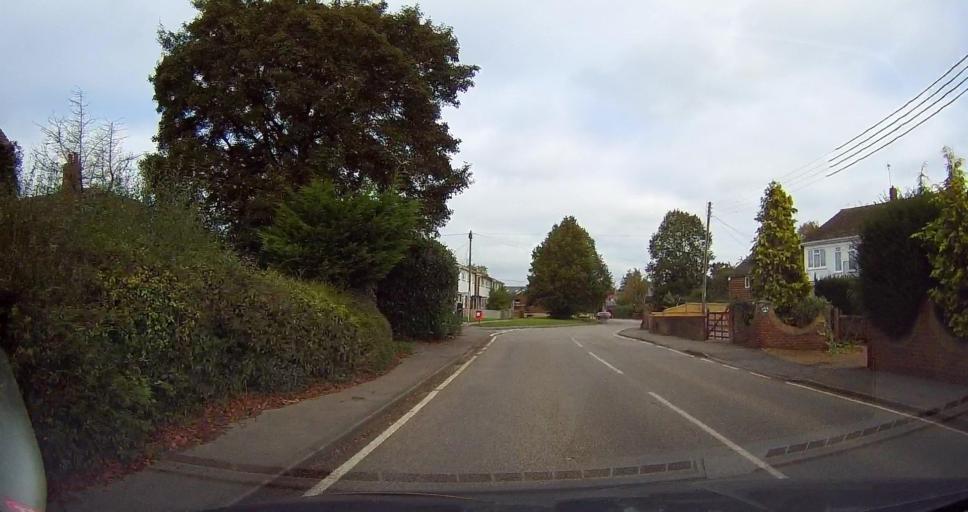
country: GB
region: England
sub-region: Kent
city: East Peckham
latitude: 51.2172
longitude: 0.3938
